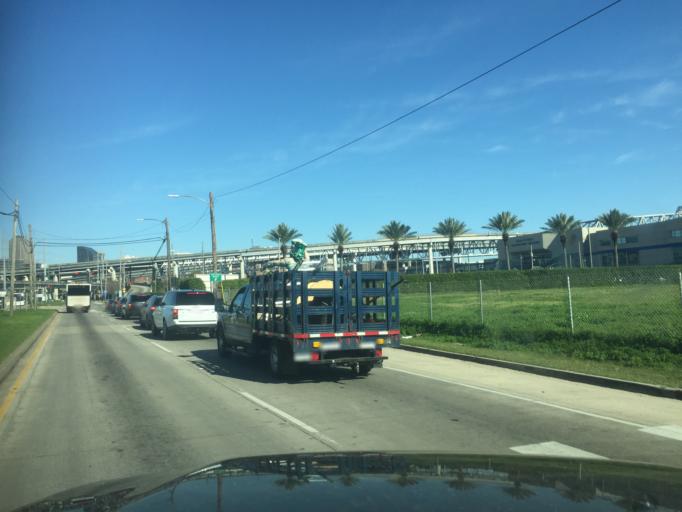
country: US
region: Louisiana
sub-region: Orleans Parish
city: New Orleans
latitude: 29.9341
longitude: -90.0662
